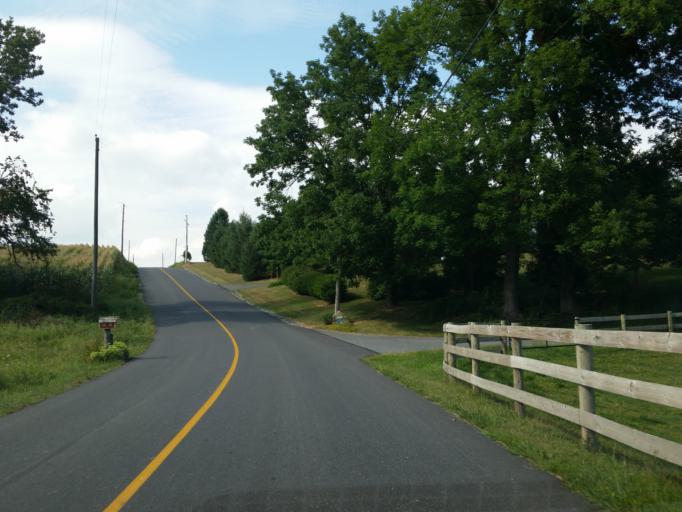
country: US
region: Pennsylvania
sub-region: Lancaster County
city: Mount Joy
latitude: 40.1444
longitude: -76.4642
